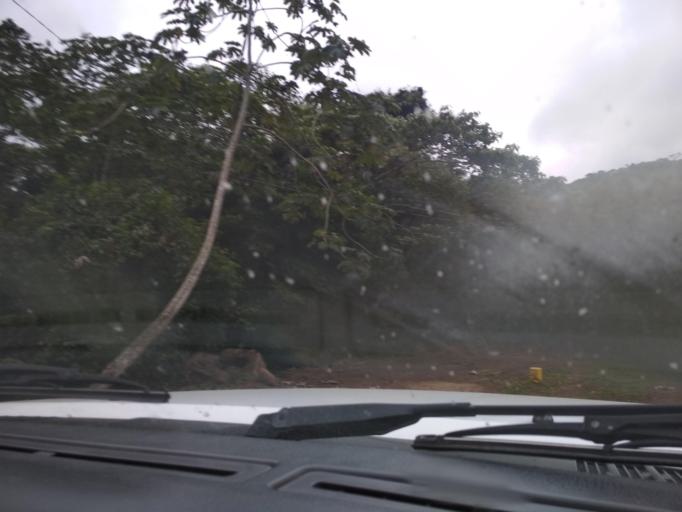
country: MX
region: Veracruz
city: El Castillo
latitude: 19.5653
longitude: -96.8474
